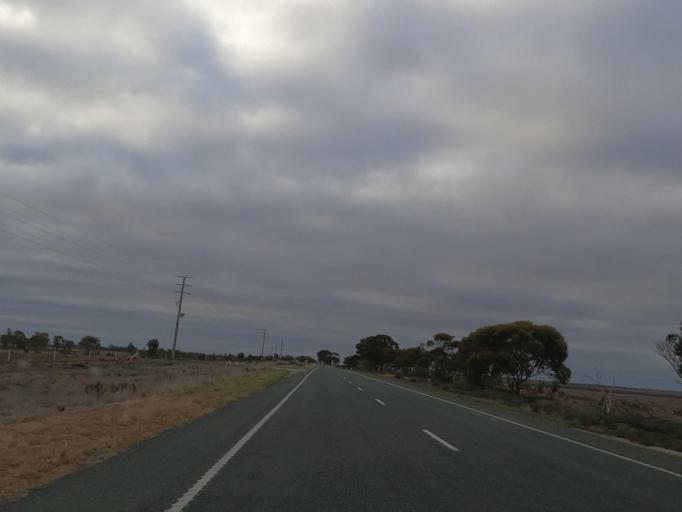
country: AU
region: Victoria
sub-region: Swan Hill
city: Swan Hill
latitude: -35.5789
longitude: 143.7888
